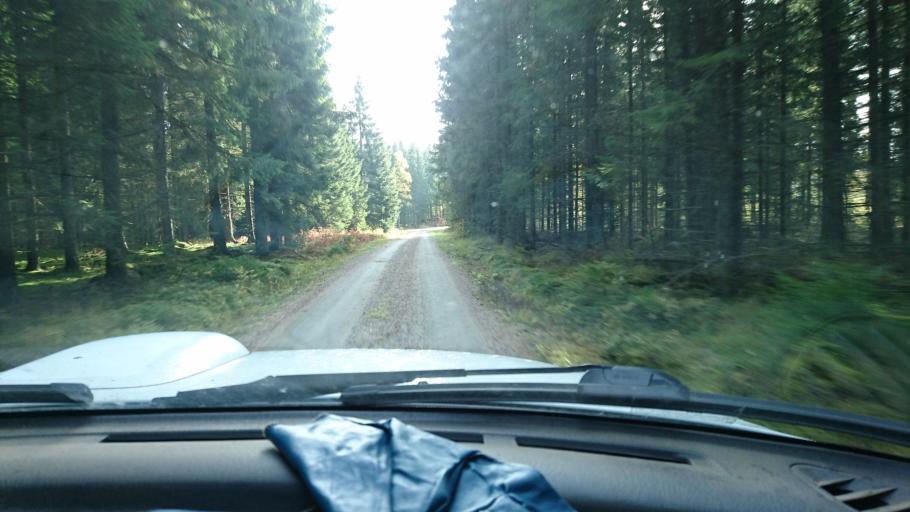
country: SE
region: Vaestra Goetaland
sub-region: Ulricehamns Kommun
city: Ulricehamn
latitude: 57.9465
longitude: 13.5388
